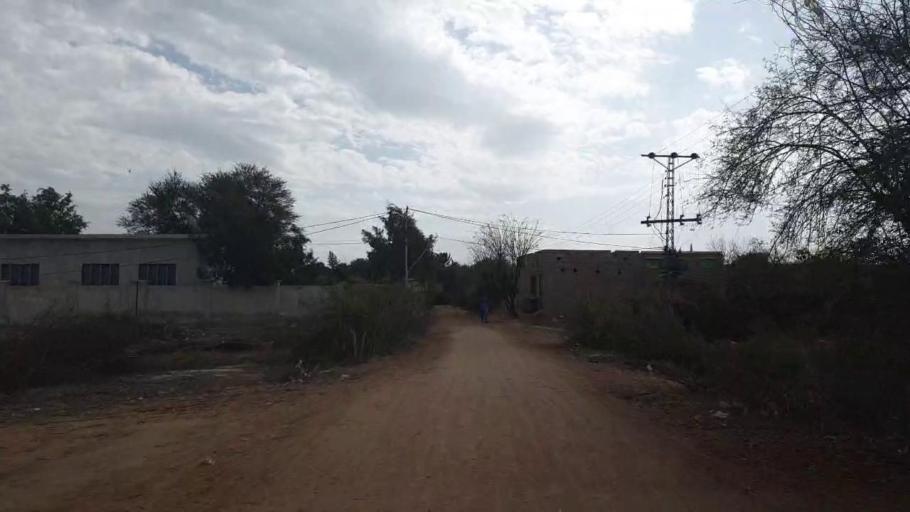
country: PK
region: Sindh
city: Hala
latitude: 25.9303
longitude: 68.4534
